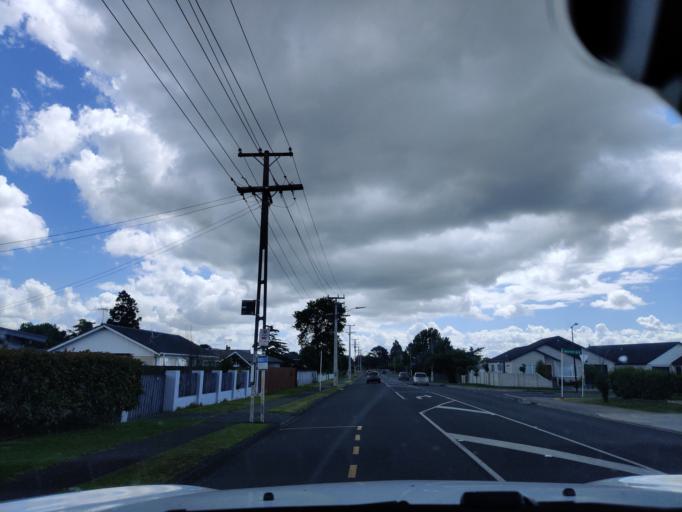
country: NZ
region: Auckland
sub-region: Auckland
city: Red Hill
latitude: -37.0536
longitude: 174.9640
